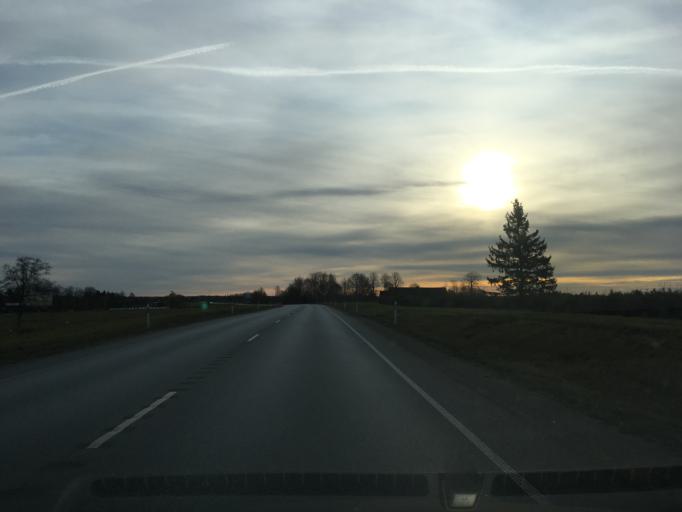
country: EE
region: Ida-Virumaa
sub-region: Kivioli linn
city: Kivioli
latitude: 59.4164
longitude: 26.9775
